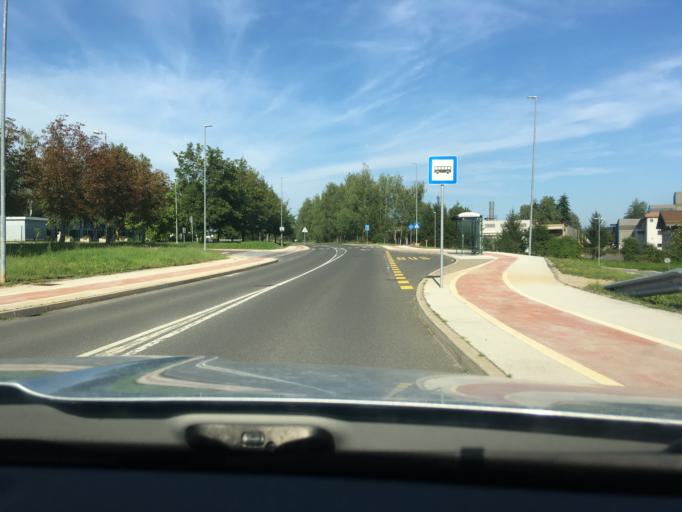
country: SI
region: Crnomelj
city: Crnomelj
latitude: 45.5722
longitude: 15.1813
